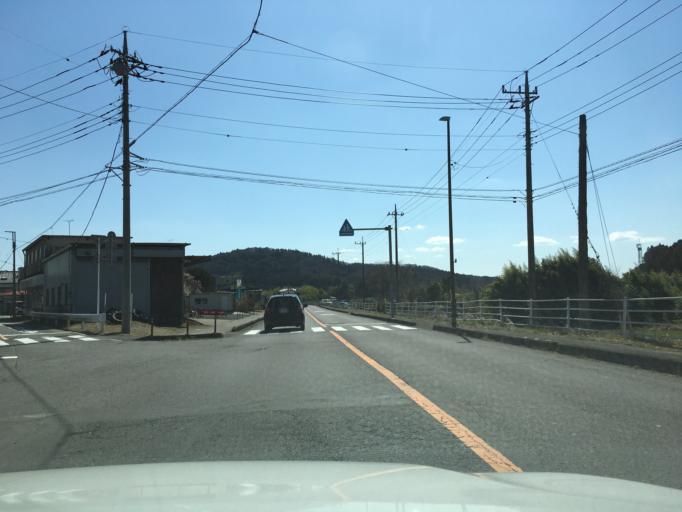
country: JP
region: Tochigi
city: Kuroiso
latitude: 36.9602
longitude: 140.1553
